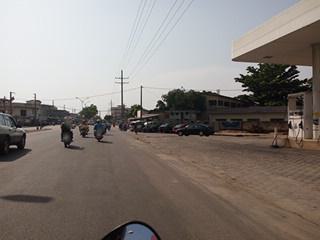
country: BJ
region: Littoral
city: Cotonou
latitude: 6.3711
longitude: 2.4159
